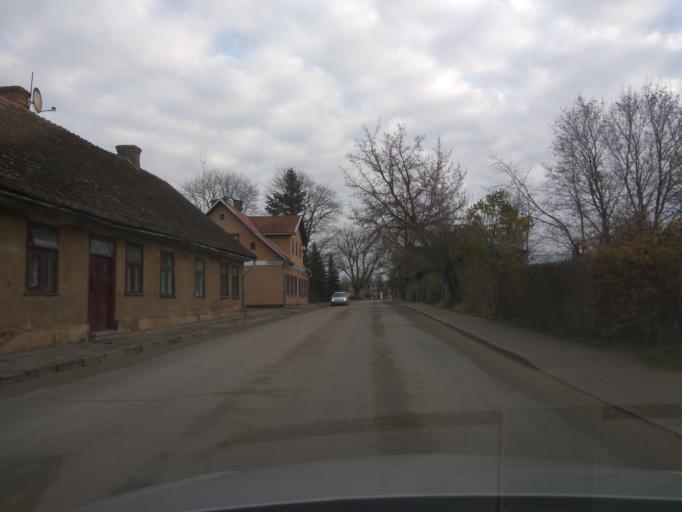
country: LV
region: Kuldigas Rajons
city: Kuldiga
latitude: 56.9640
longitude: 21.9786
